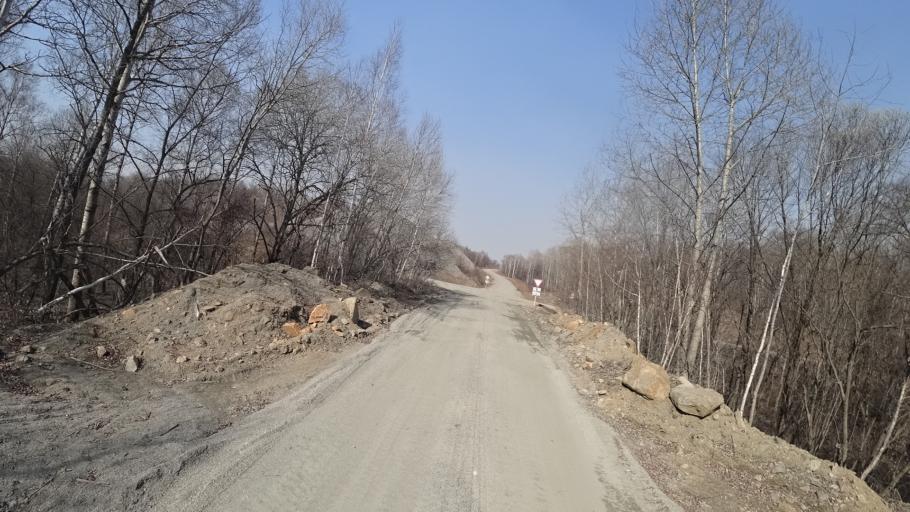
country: RU
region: Amur
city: Novobureyskiy
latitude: 49.7963
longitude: 129.9567
